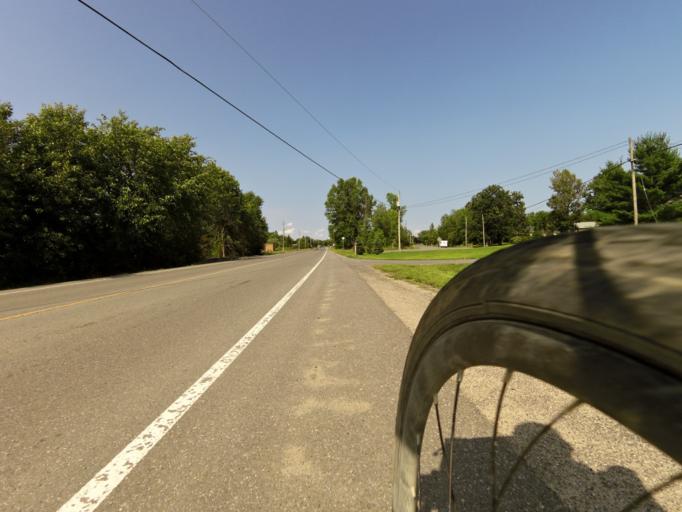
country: CA
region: Ontario
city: Skatepark
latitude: 44.2701
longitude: -76.7174
